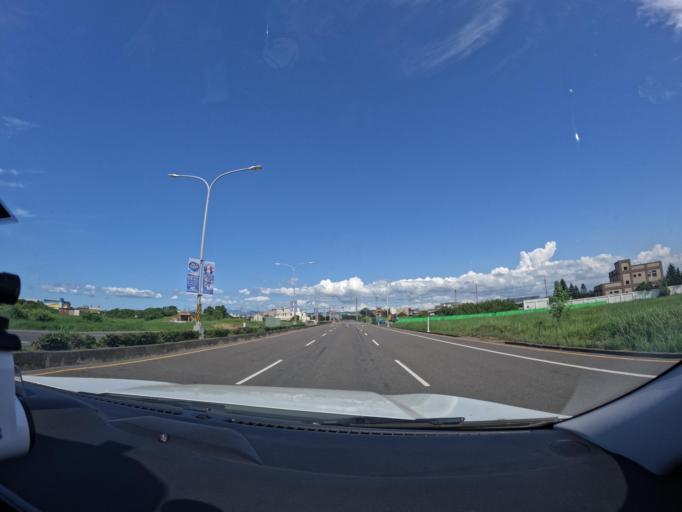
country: TW
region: Taiwan
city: Taoyuan City
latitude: 25.1072
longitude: 121.2357
